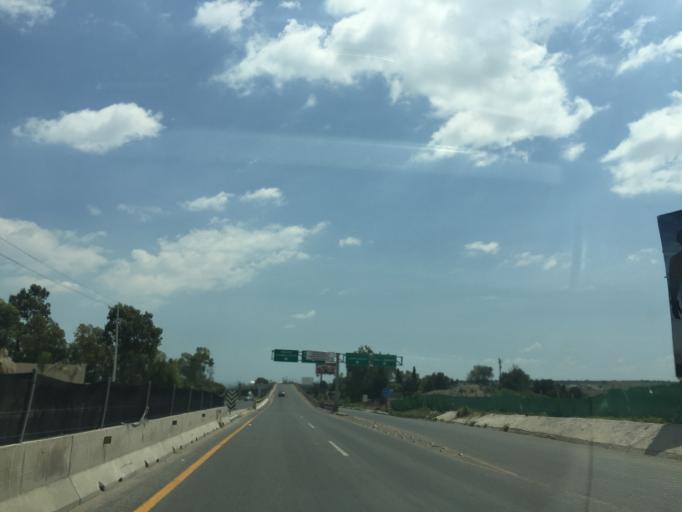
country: MX
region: Guanajuato
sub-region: Leon
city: Fraccionamiento Paseo de las Torres
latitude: 21.1814
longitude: -101.7430
